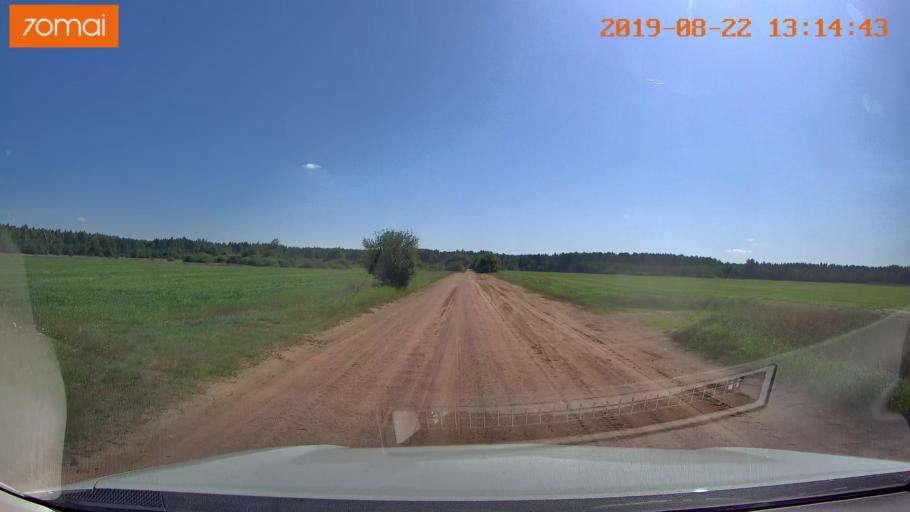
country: BY
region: Minsk
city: Prawdzinski
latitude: 53.2653
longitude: 27.8903
